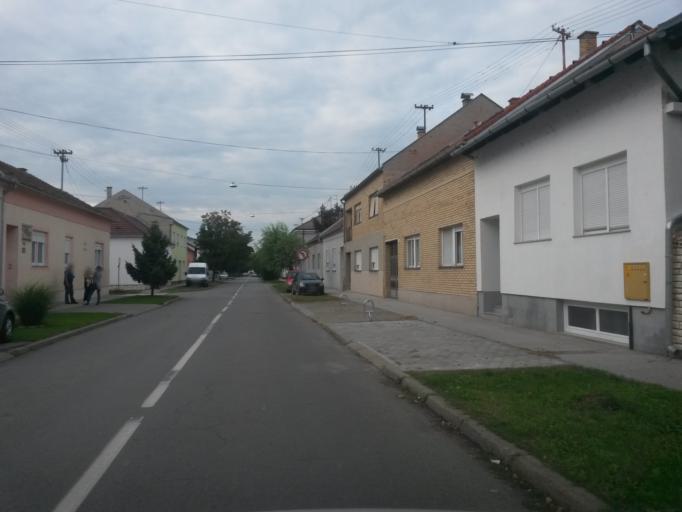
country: HR
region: Osjecko-Baranjska
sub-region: Grad Osijek
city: Osijek
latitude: 45.5476
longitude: 18.6824
